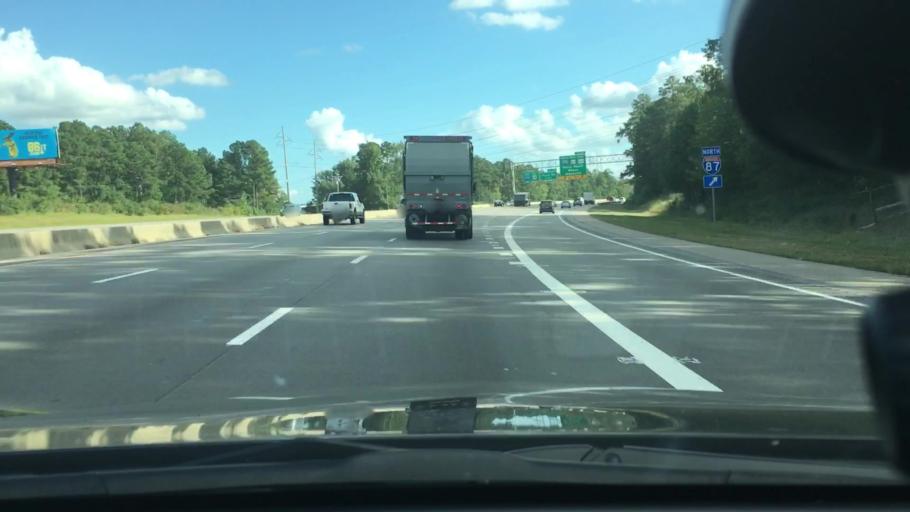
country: US
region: North Carolina
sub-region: Wake County
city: Raleigh
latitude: 35.7894
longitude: -78.5757
